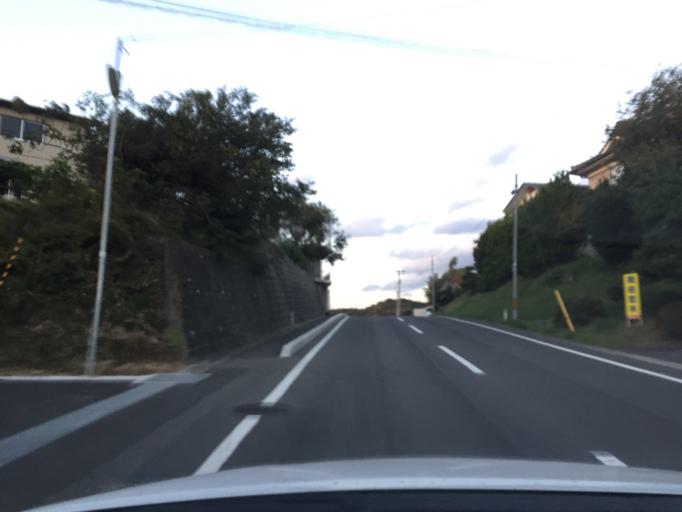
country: JP
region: Fukushima
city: Miharu
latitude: 37.4589
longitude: 140.4392
